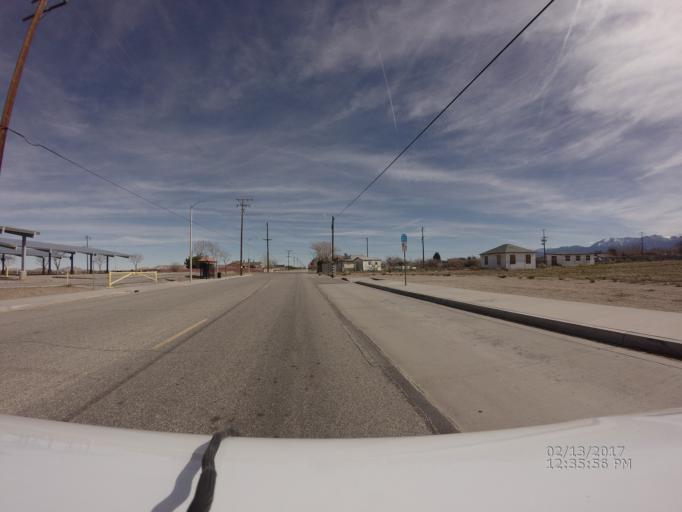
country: US
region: California
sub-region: Los Angeles County
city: Littlerock
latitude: 34.5727
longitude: -117.9355
